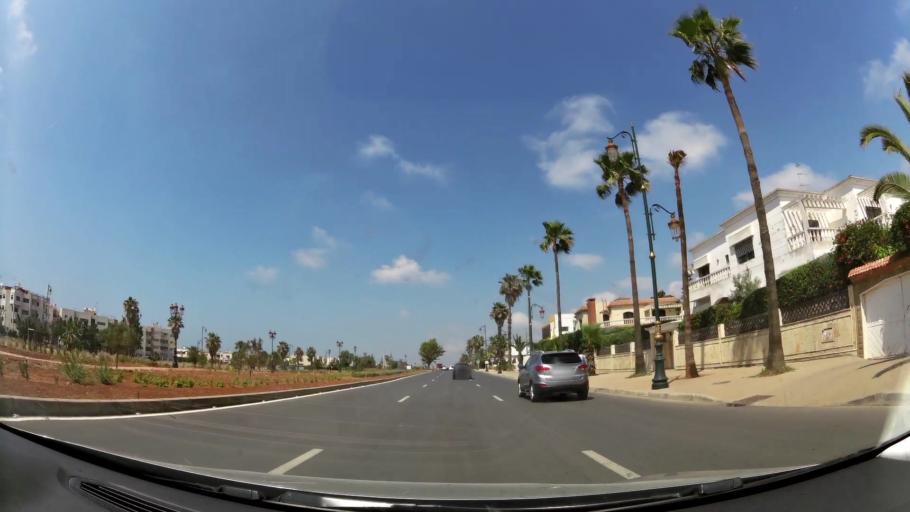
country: MA
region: Rabat-Sale-Zemmour-Zaer
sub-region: Skhirate-Temara
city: Temara
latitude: 33.9586
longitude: -6.8766
